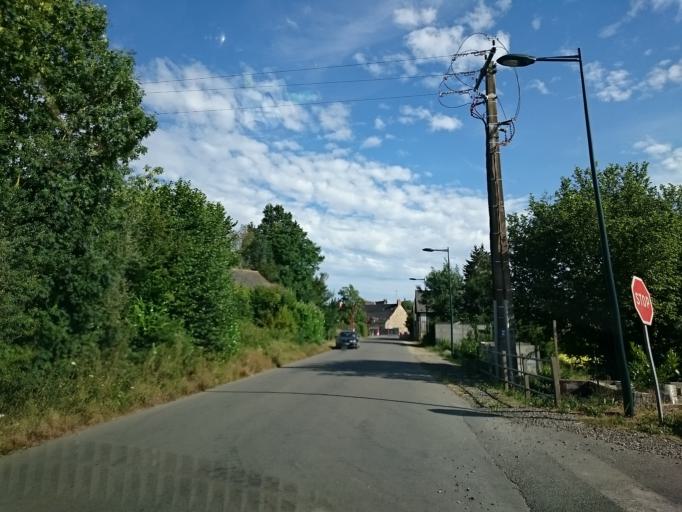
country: FR
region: Brittany
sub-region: Departement d'Ille-et-Vilaine
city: Pance
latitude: 47.8977
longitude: -1.6138
